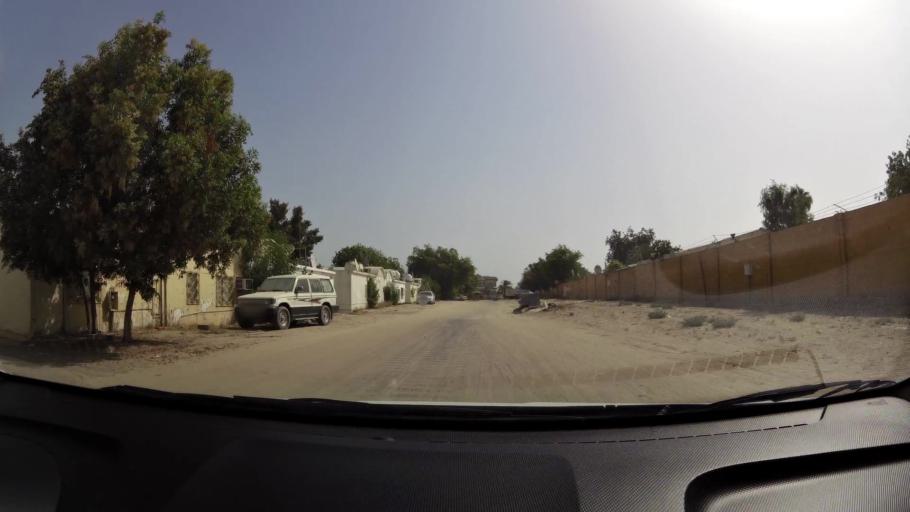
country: AE
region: Ash Shariqah
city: Sharjah
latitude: 25.3421
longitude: 55.4150
